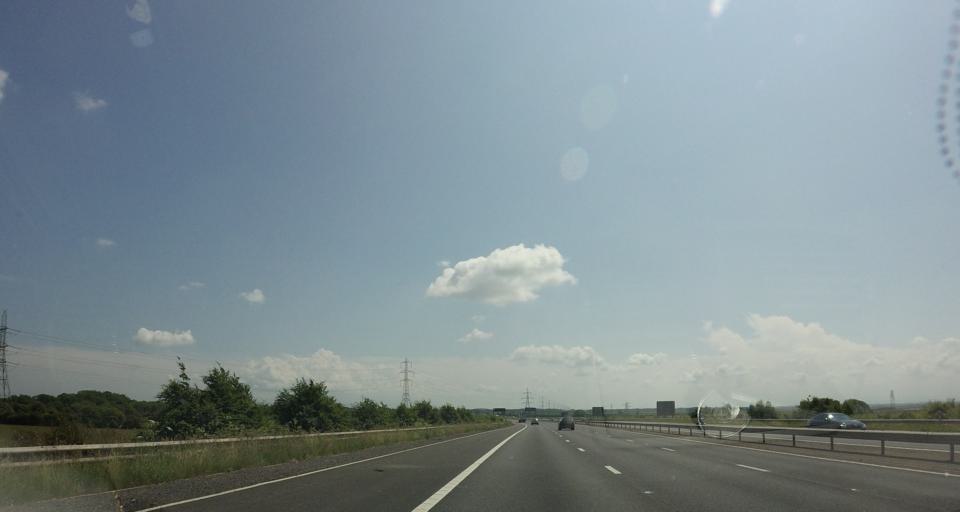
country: GB
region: Scotland
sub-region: Dumfries and Galloway
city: Gretna
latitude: 54.9889
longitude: -3.0399
